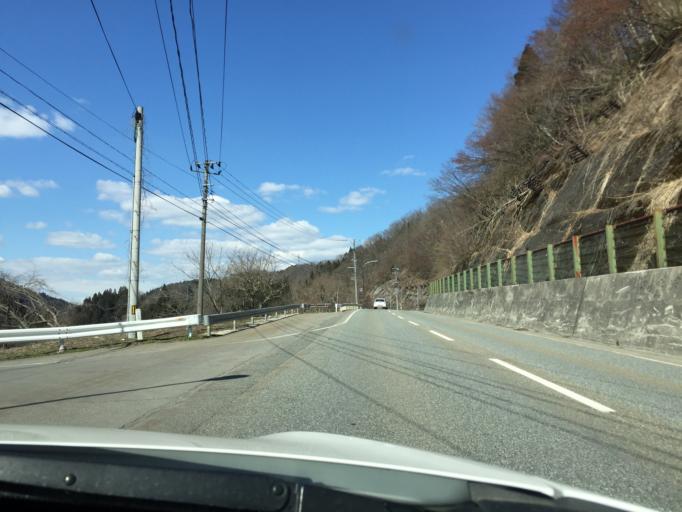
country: JP
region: Yamagata
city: Nagai
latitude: 38.2490
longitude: 140.1045
